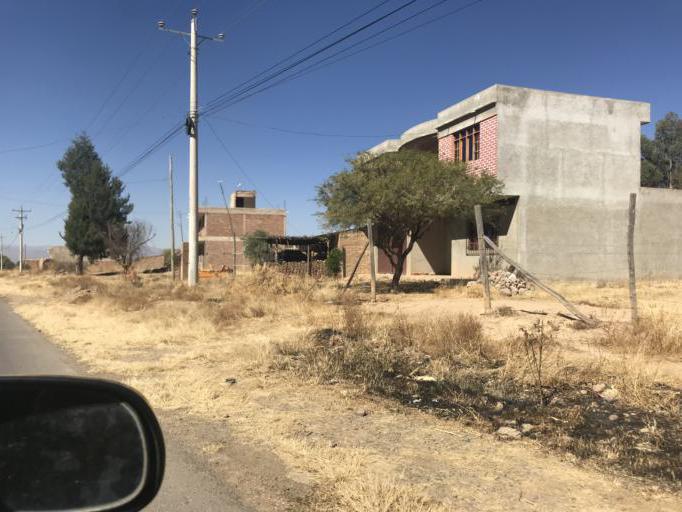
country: BO
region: Cochabamba
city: Cliza
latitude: -17.6019
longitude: -65.9757
